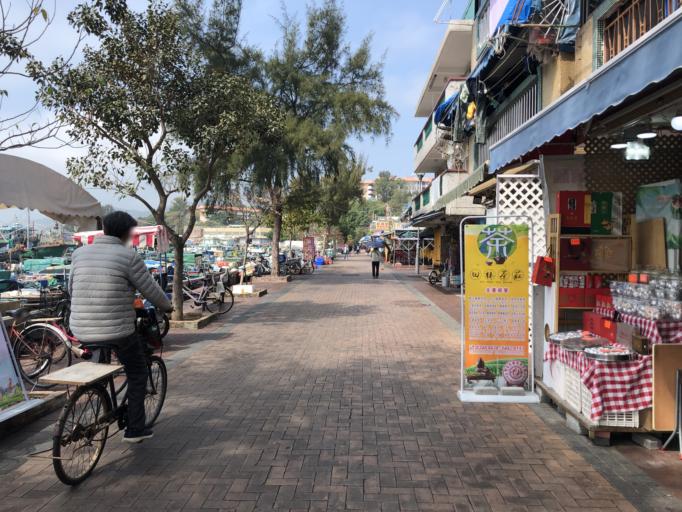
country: HK
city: Yung Shue Wan
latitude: 22.2108
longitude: 114.0279
